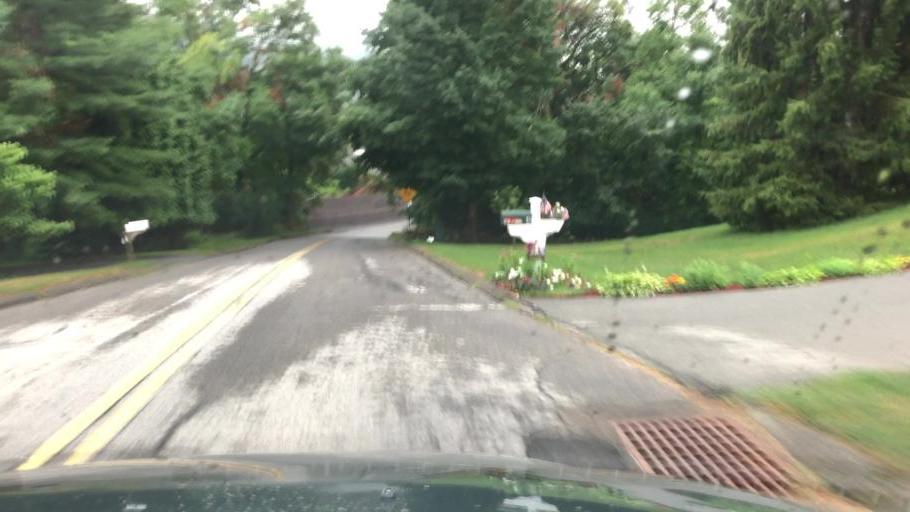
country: US
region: New York
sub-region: Dutchess County
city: Fishkill
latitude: 41.5313
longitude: -73.9190
